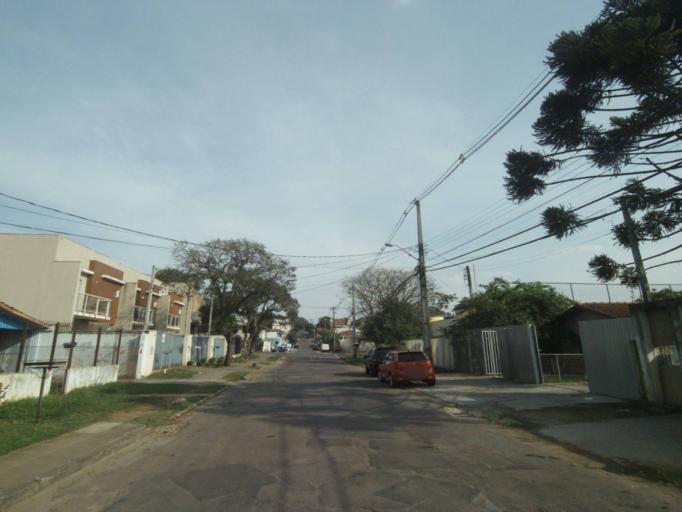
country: BR
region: Parana
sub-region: Curitiba
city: Curitiba
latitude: -25.4613
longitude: -49.3163
